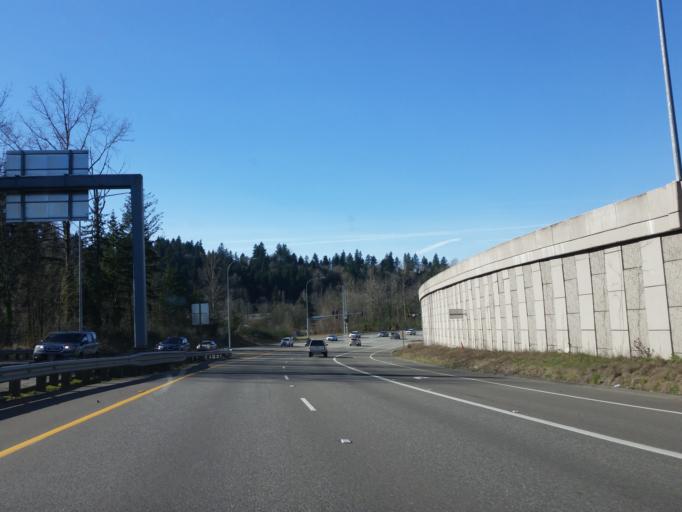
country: US
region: Washington
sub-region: King County
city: Bothell
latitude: 47.7558
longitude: -122.1915
